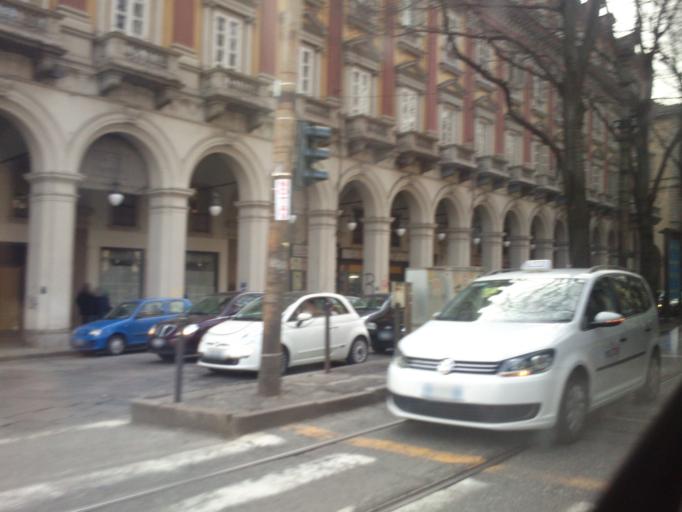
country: IT
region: Piedmont
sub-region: Provincia di Torino
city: Turin
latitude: 45.0764
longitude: 7.6699
